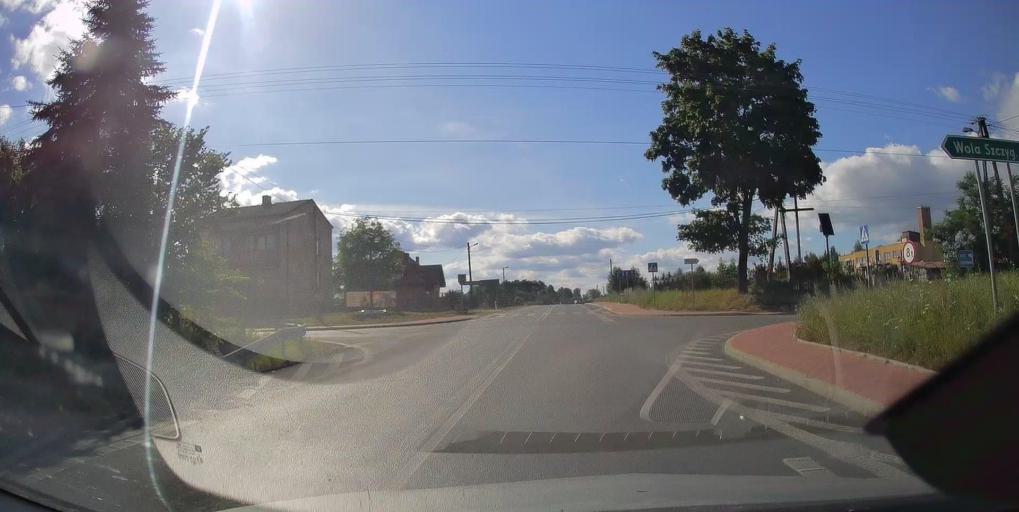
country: PL
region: Swietokrzyskie
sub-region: Powiat kielecki
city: Bodzentyn
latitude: 50.9361
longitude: 20.9588
